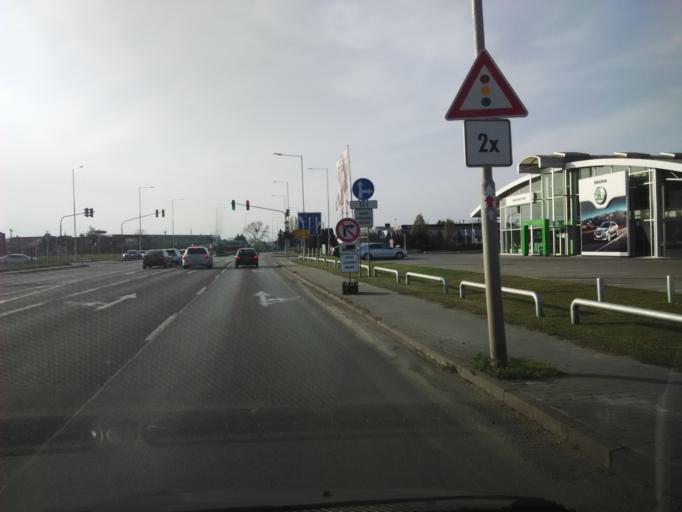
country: SK
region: Nitriansky
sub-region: Okres Nove Zamky
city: Nove Zamky
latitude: 48.0020
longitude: 18.1595
